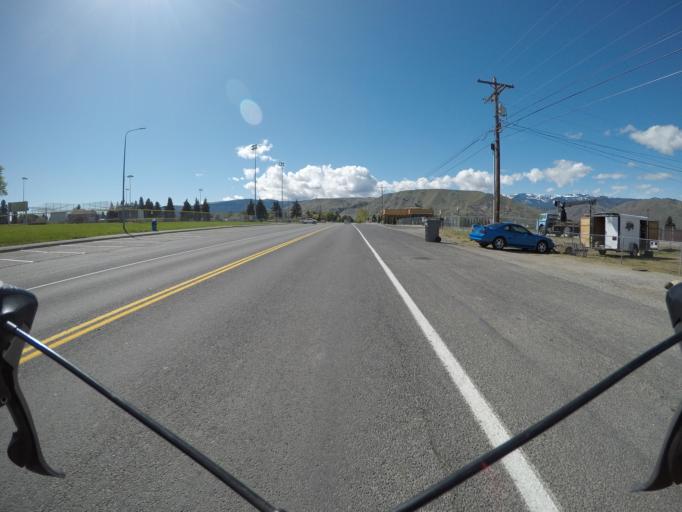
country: US
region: Washington
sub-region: Douglas County
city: East Wenatchee
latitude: 47.4076
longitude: -120.2772
